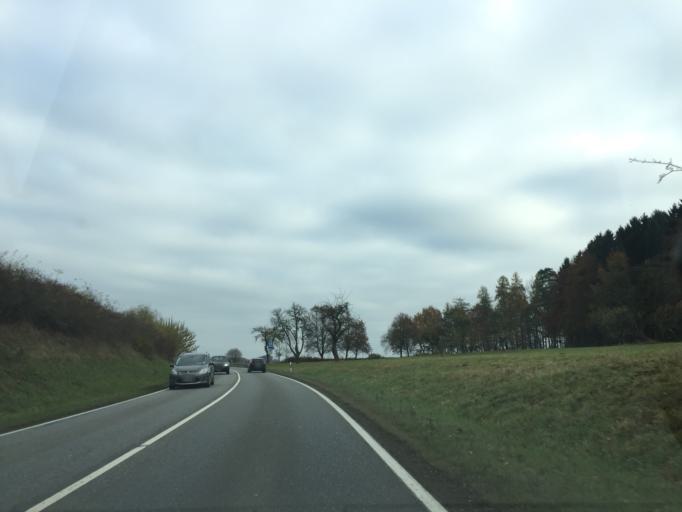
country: DE
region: Rheinland-Pfalz
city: Grossholbach
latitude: 50.4435
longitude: 7.8946
